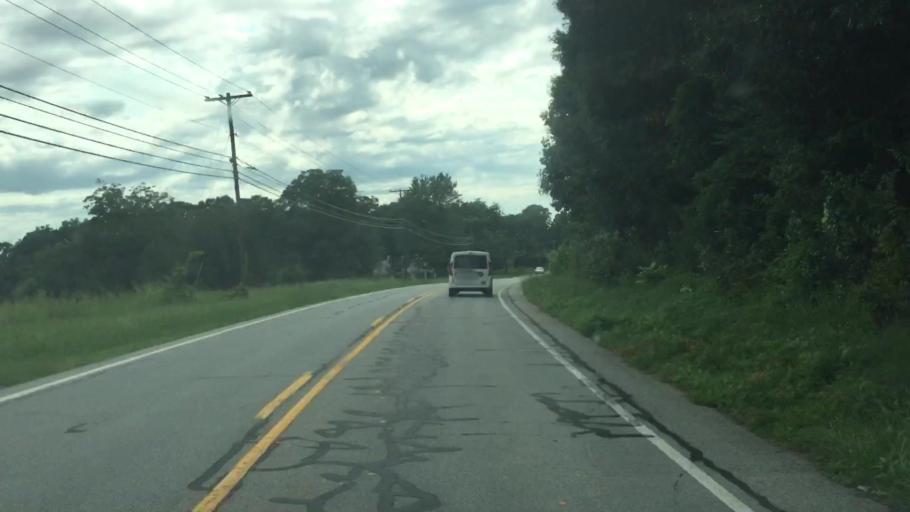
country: US
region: North Carolina
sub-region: Rowan County
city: Franklin
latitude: 35.6592
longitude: -80.5657
